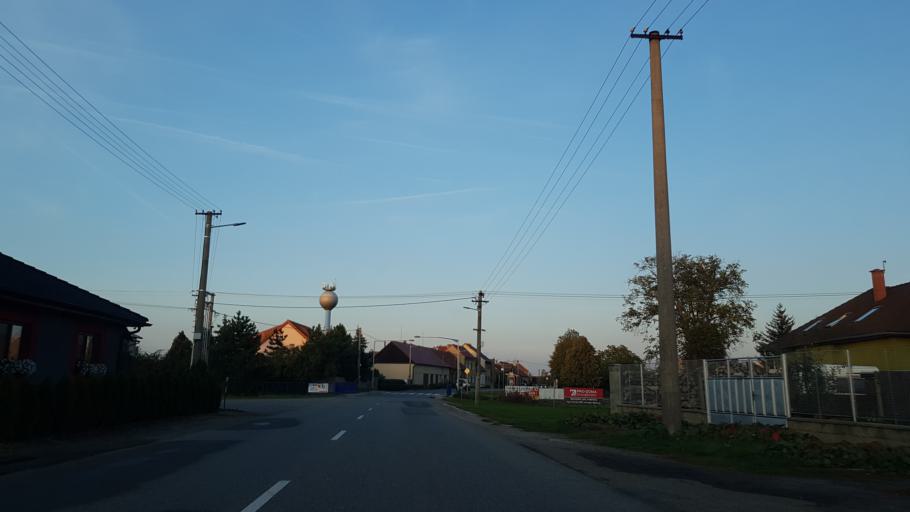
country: CZ
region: Zlin
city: Nedakonice
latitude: 49.0311
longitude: 17.3778
